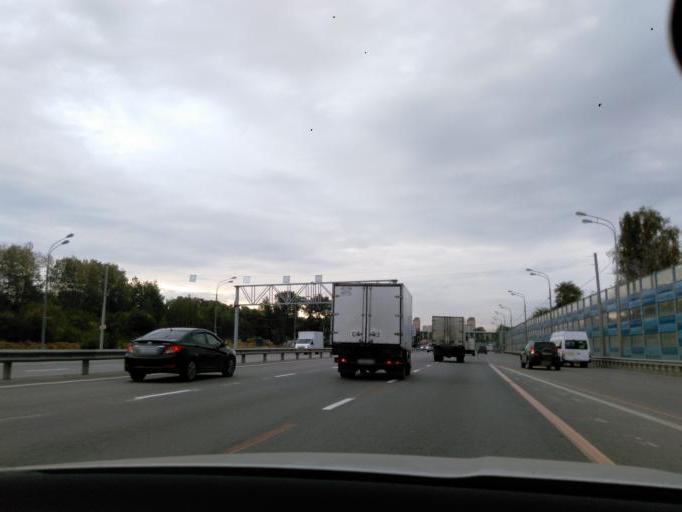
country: RU
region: Moscow
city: Severnyy
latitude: 55.9457
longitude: 37.5415
